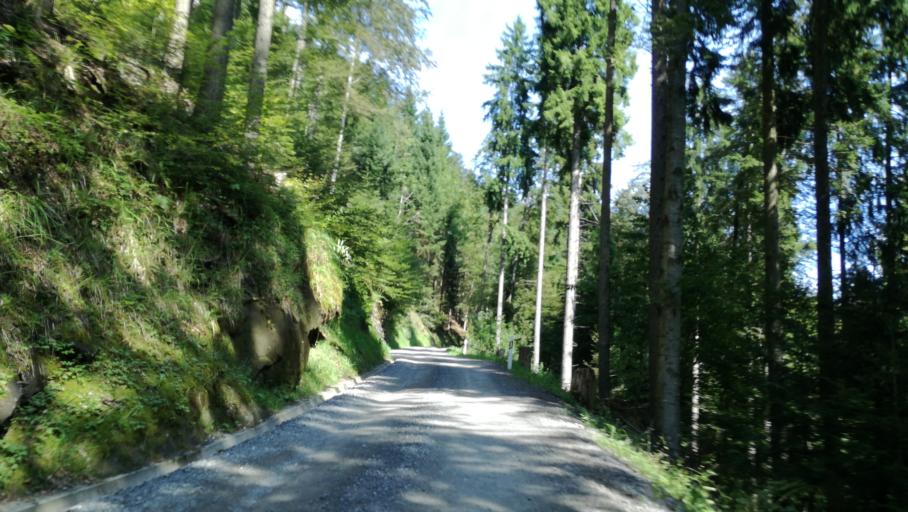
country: CH
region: Zug
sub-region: Zug
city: Unterageri
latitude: 47.1419
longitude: 8.5964
